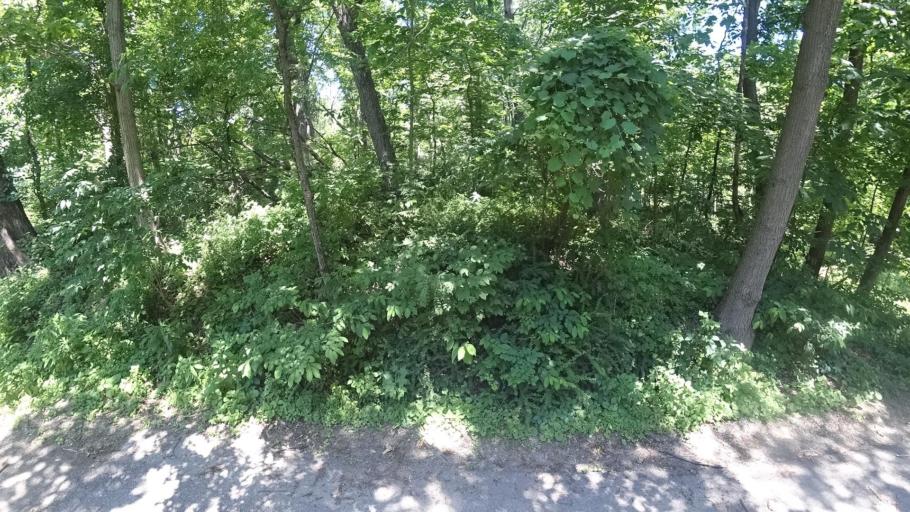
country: US
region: Indiana
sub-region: Porter County
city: Burns Harbor
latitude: 41.6068
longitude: -87.1414
